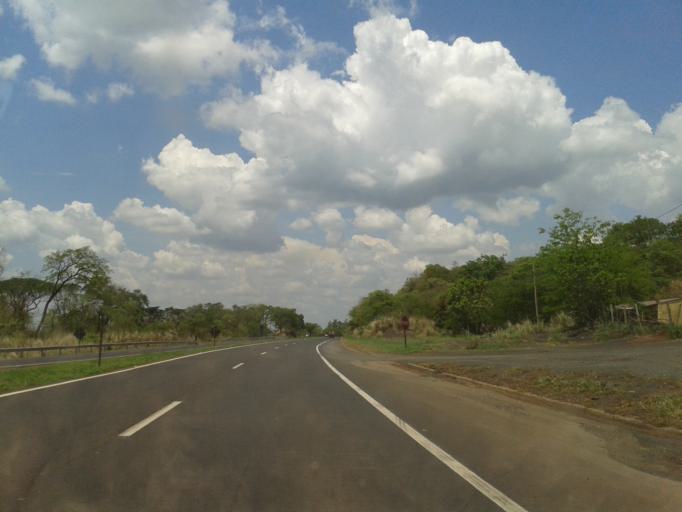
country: BR
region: Minas Gerais
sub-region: Araguari
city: Araguari
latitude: -18.7265
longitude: -48.2063
